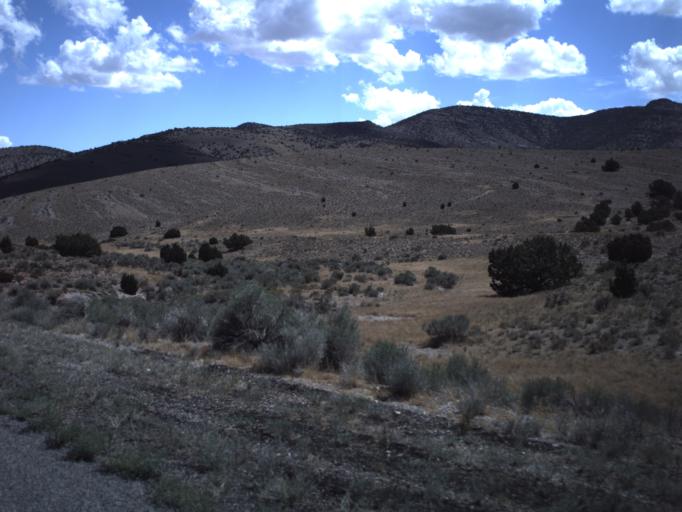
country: US
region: Utah
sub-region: Beaver County
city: Milford
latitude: 39.0771
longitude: -113.6230
